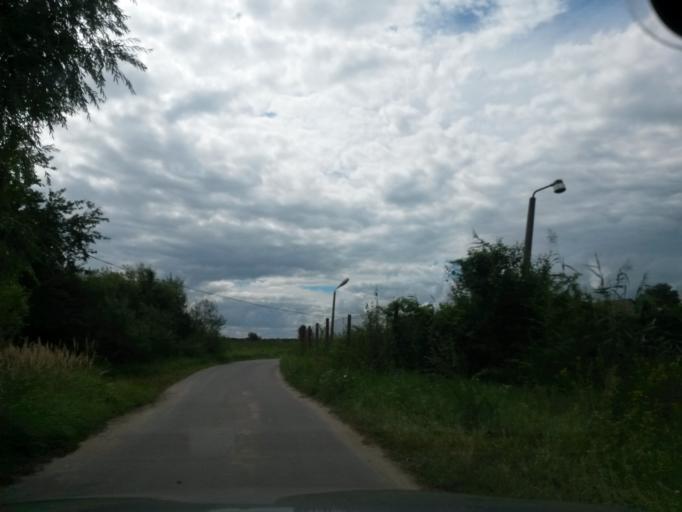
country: DE
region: Brandenburg
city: Oderberg
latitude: 52.8633
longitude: 14.0757
